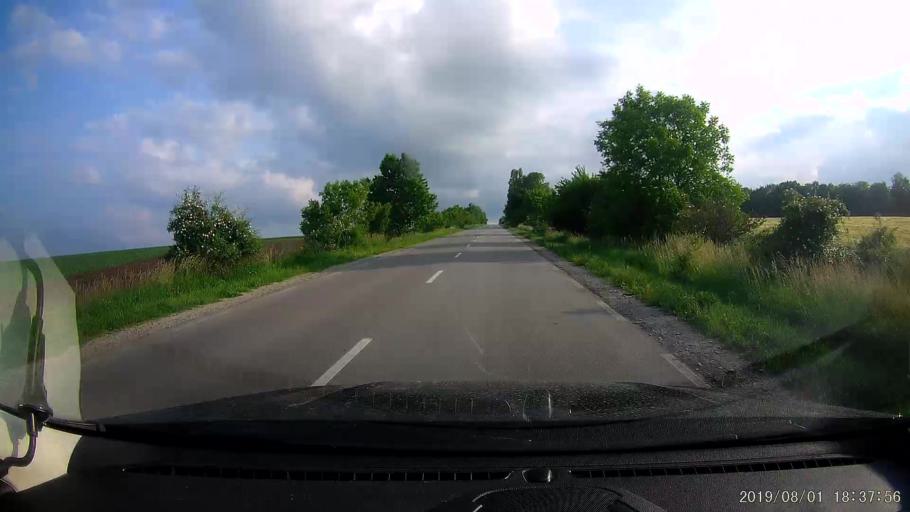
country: BG
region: Shumen
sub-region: Obshtina Khitrino
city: Gara Khitrino
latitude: 43.4109
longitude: 26.9232
